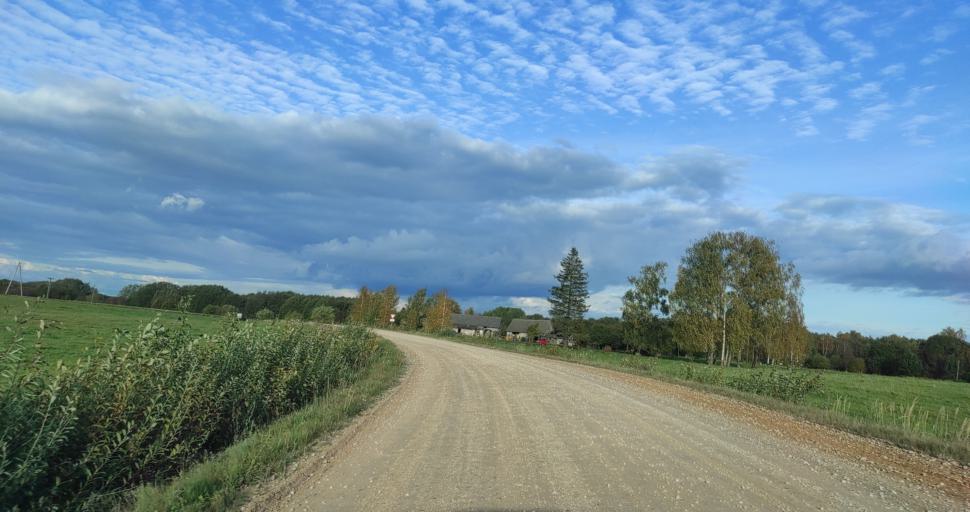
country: LV
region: Aizpute
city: Aizpute
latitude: 56.7496
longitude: 21.7903
